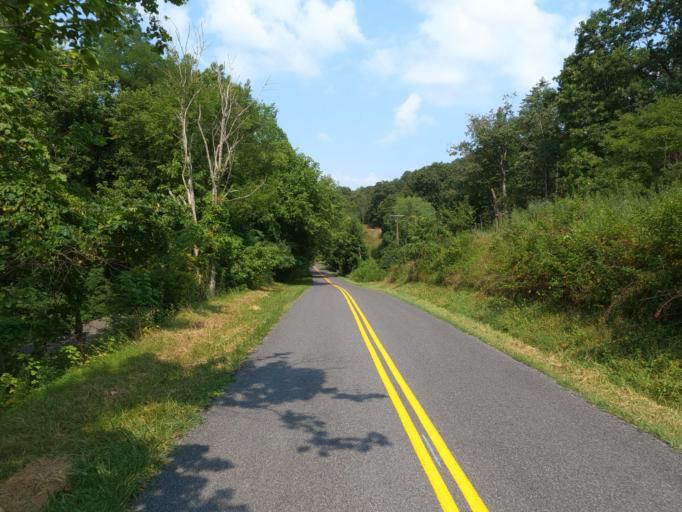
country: US
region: West Virginia
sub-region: Morgan County
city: Berkeley Springs
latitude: 39.6315
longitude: -78.3070
